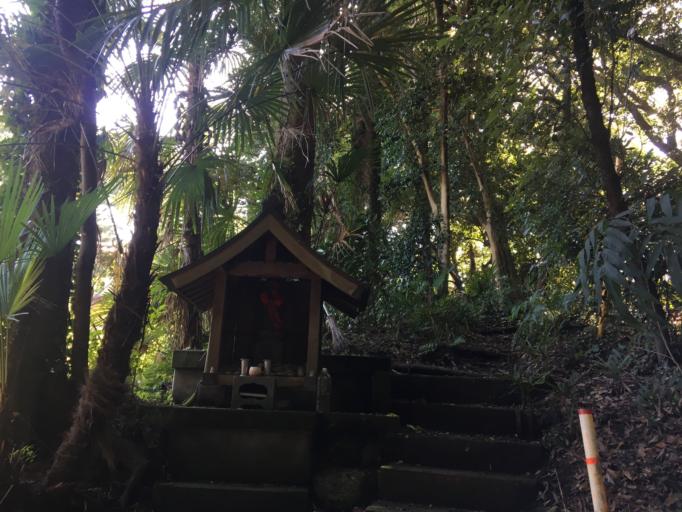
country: JP
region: Kanagawa
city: Yokohama
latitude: 35.5272
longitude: 139.5716
